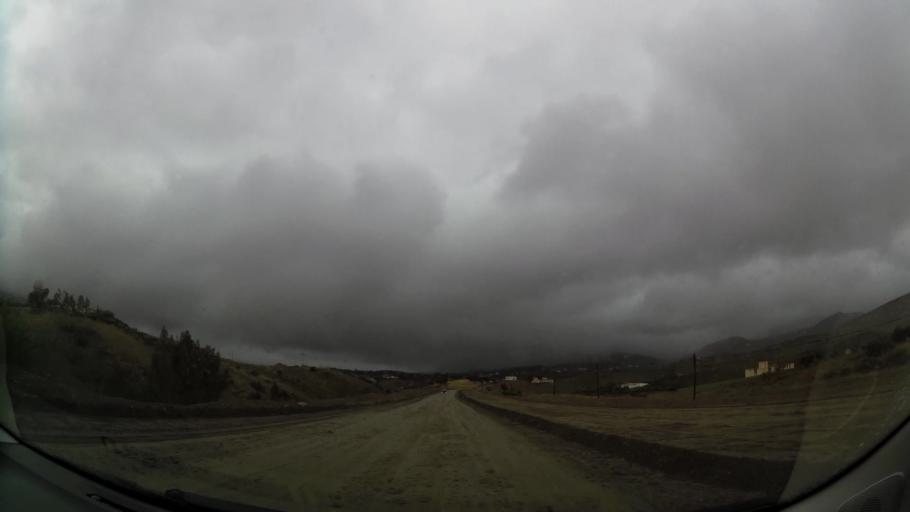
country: MA
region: Oriental
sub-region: Nador
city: Midar
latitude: 34.8949
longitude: -3.7680
